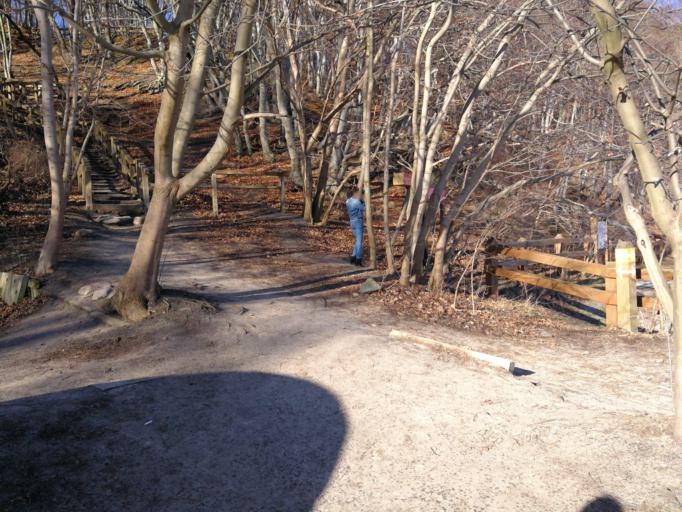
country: PL
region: Pomeranian Voivodeship
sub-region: Sopot
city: Sopot
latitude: 54.4826
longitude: 18.5653
